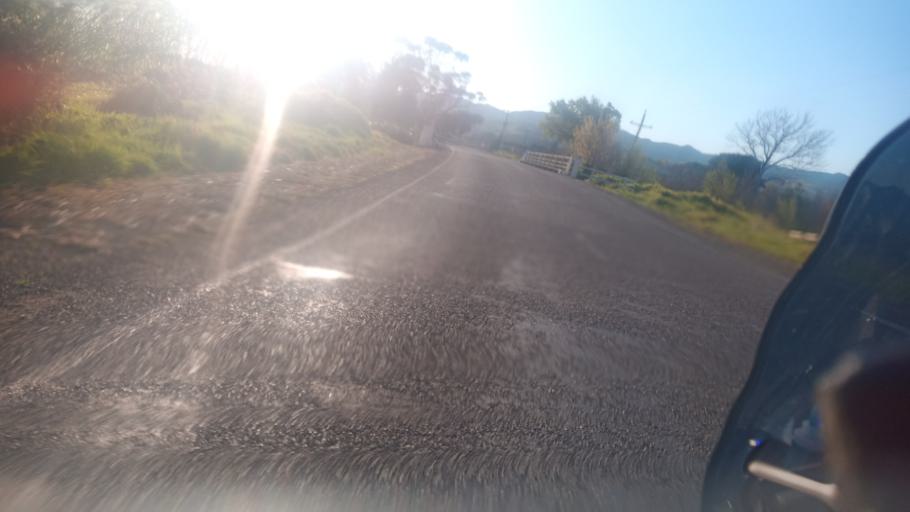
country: NZ
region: Hawke's Bay
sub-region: Wairoa District
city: Wairoa
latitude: -39.0471
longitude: 177.7571
